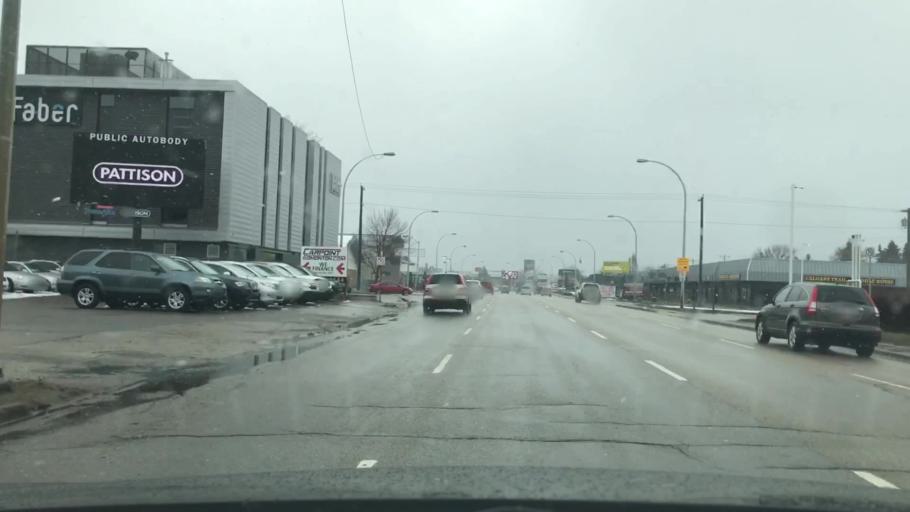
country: CA
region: Alberta
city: Edmonton
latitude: 53.4959
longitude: -113.4977
